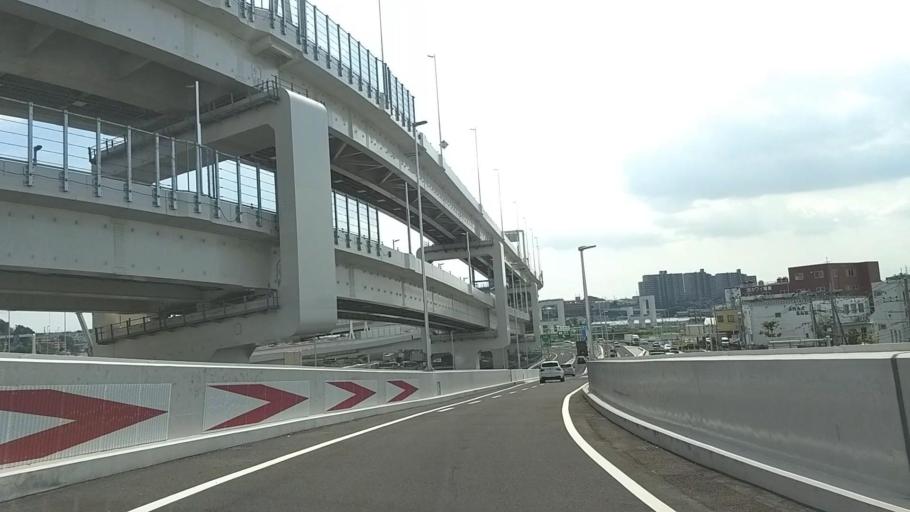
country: JP
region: Kanagawa
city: Yokohama
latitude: 35.5182
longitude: 139.5917
